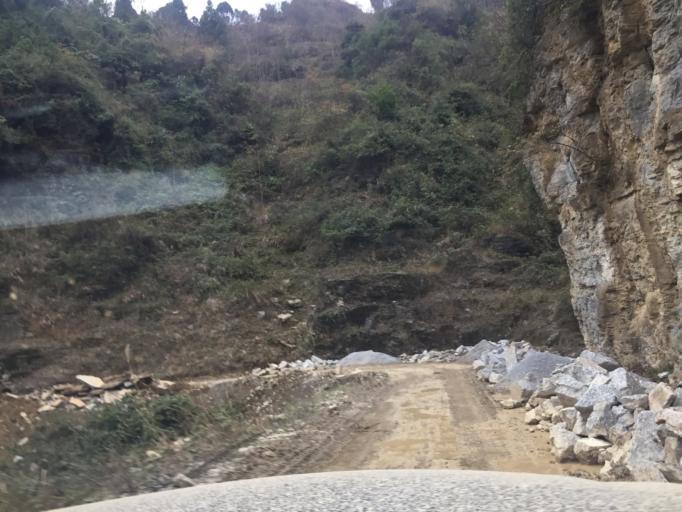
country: CN
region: Guizhou Sheng
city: Changfeng
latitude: 28.4799
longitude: 108.0726
